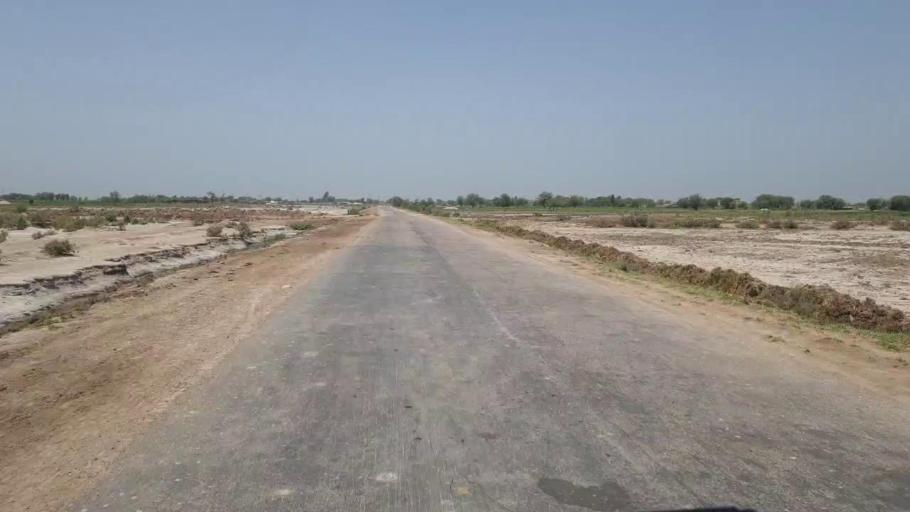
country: PK
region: Sindh
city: Nawabshah
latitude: 26.3612
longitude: 68.4056
